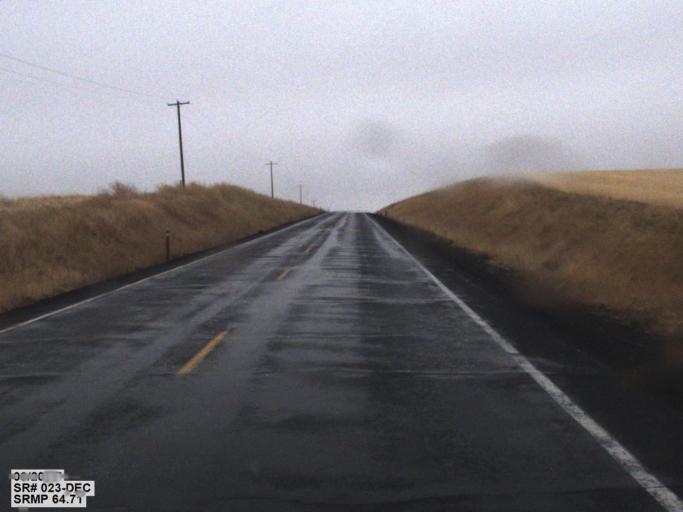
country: US
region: Washington
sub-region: Lincoln County
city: Davenport
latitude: 47.4783
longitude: -118.2373
